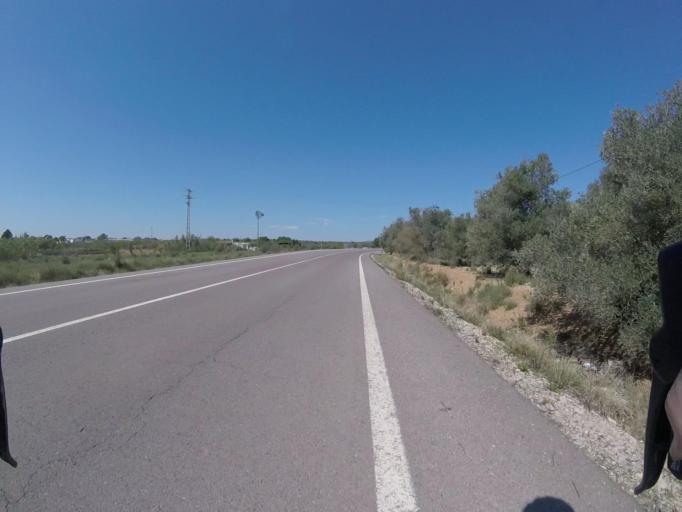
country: ES
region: Valencia
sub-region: Provincia de Castello
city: Benlloch
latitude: 40.2267
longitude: 0.0574
